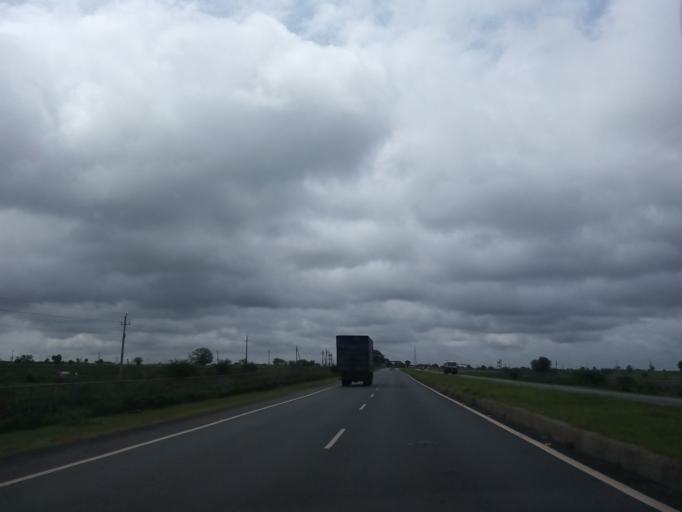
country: IN
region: Karnataka
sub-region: Haveri
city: Haveri
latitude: 14.8290
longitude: 75.3643
